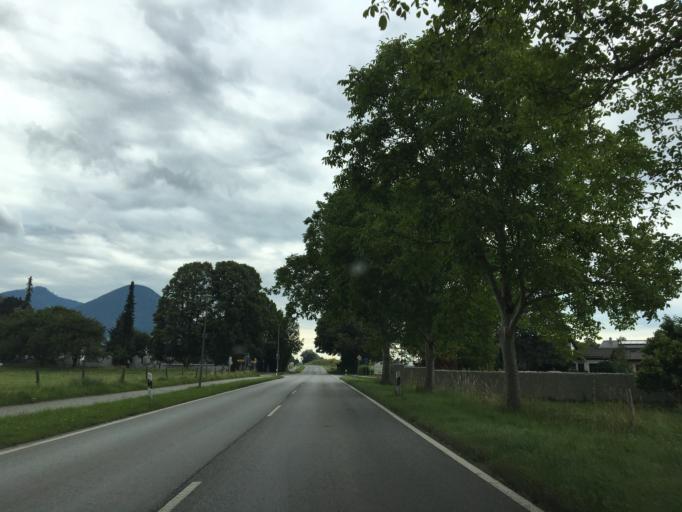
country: DE
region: Bavaria
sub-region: Upper Bavaria
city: Flintsbach
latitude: 47.7261
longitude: 12.1205
